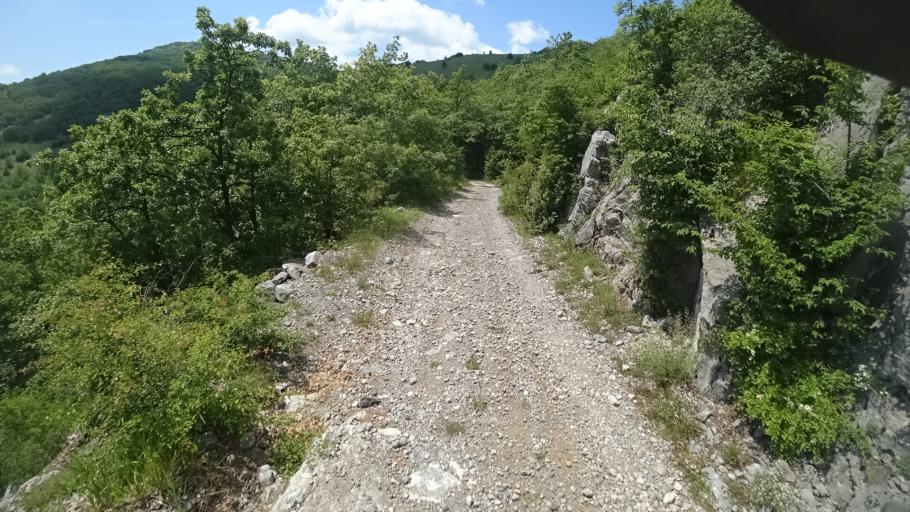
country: HR
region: Zadarska
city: Gracac
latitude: 44.4476
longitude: 15.9152
